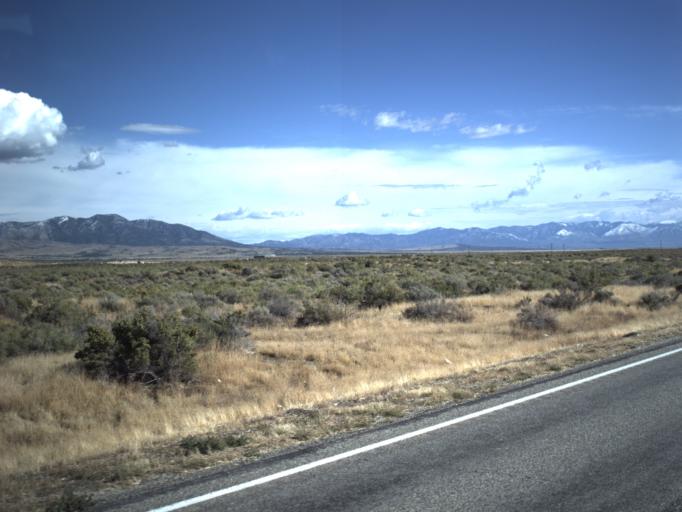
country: US
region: Utah
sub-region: Millard County
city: Delta
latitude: 39.3258
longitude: -112.4847
